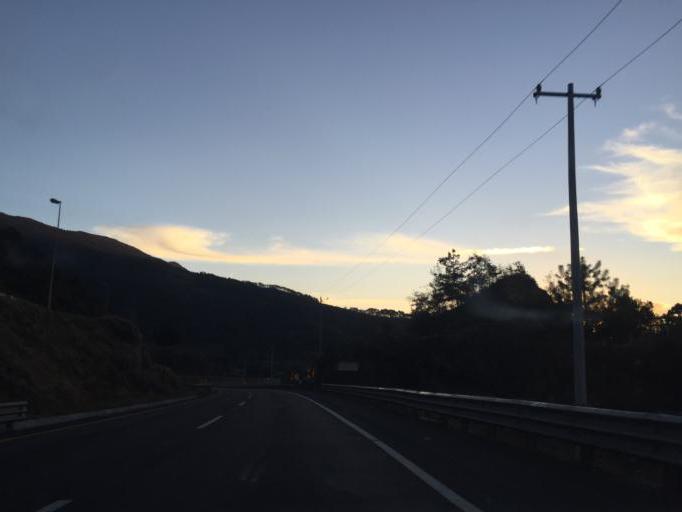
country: MX
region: Veracruz
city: Maltrata
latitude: 18.8520
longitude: -97.2631
